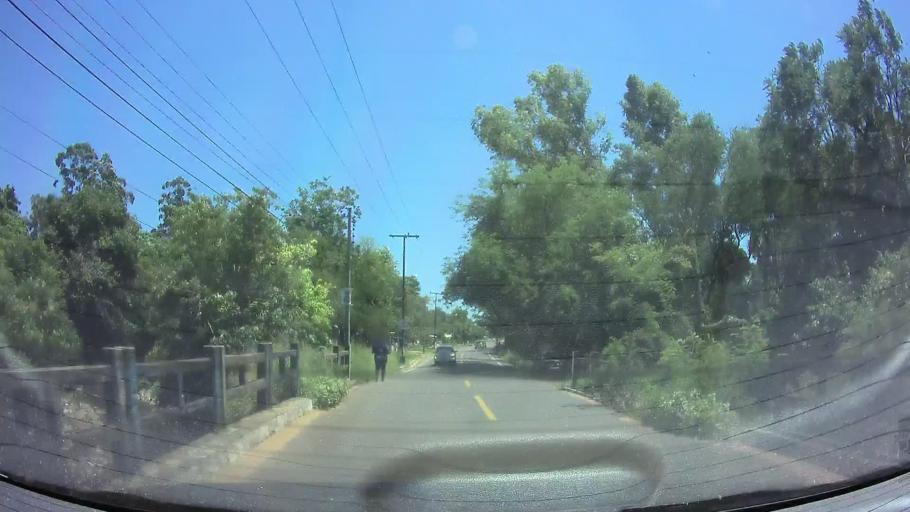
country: PY
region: Central
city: Limpio
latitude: -25.2452
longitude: -57.4912
